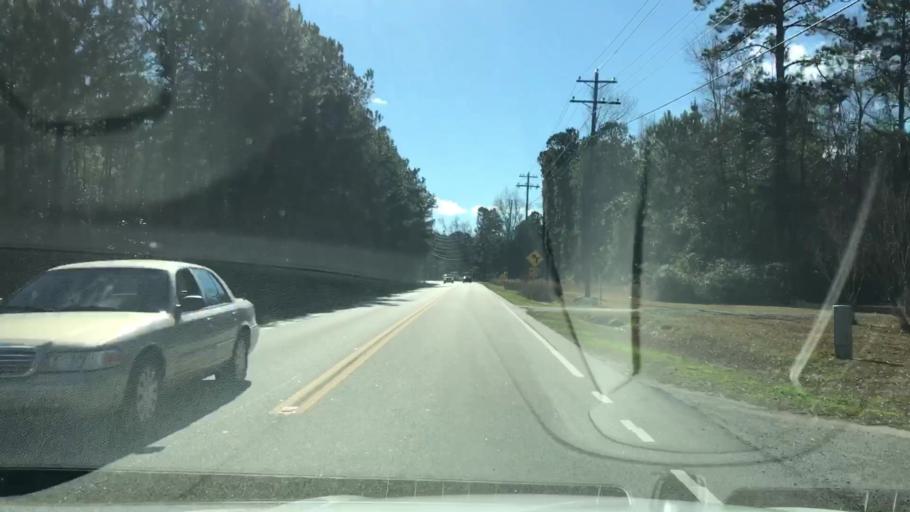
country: US
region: South Carolina
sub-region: Dorchester County
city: Summerville
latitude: 33.0702
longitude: -80.2216
